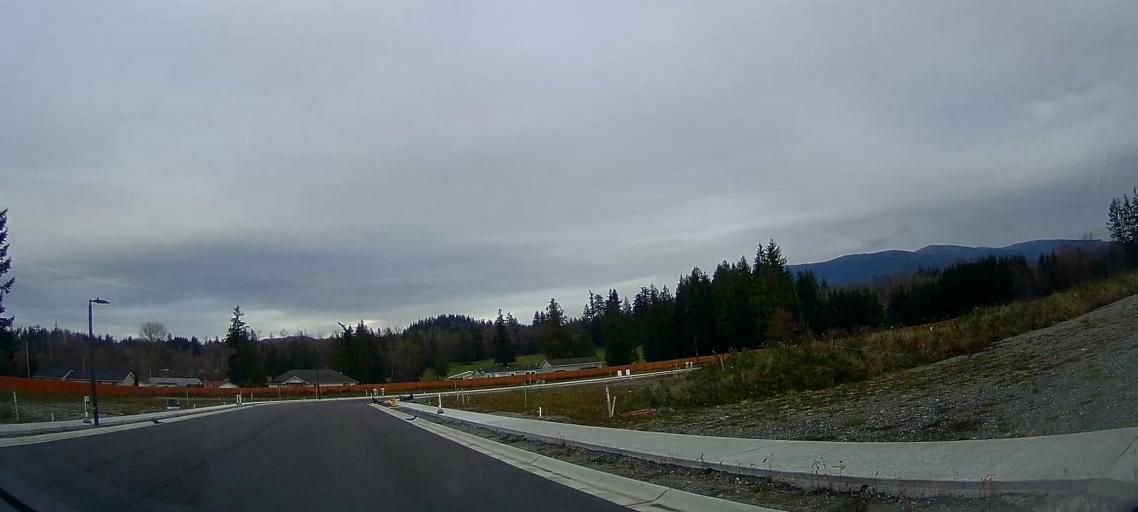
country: US
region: Washington
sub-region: Skagit County
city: Sedro-Woolley
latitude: 48.5165
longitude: -122.2465
